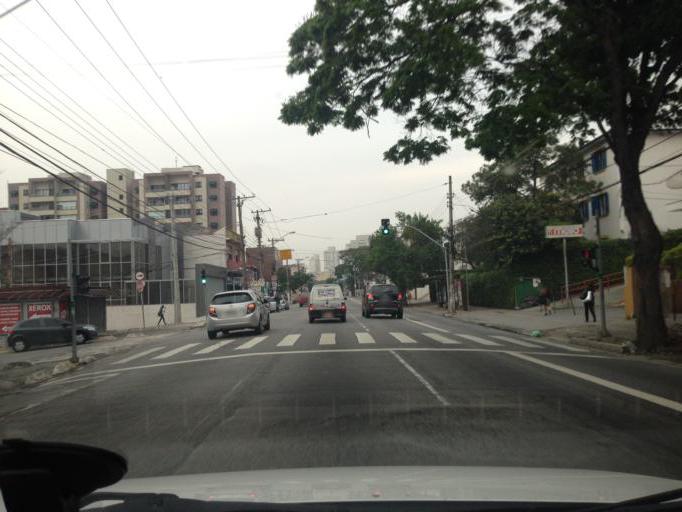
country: BR
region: Sao Paulo
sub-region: Sao Paulo
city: Sao Paulo
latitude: -23.5253
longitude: -46.7108
